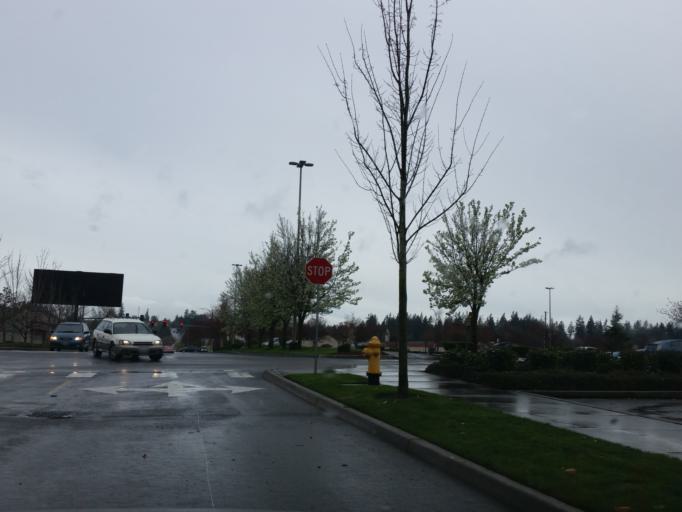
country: US
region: Washington
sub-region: Snohomish County
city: Alderwood Manor
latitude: 47.8319
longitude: -122.2663
